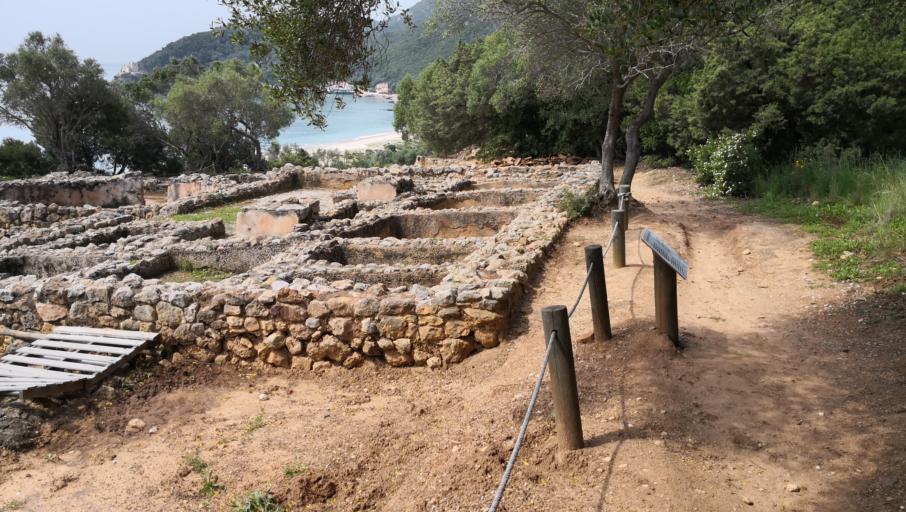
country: PT
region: Setubal
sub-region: Palmela
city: Quinta do Anjo
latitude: 38.4816
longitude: -8.9767
